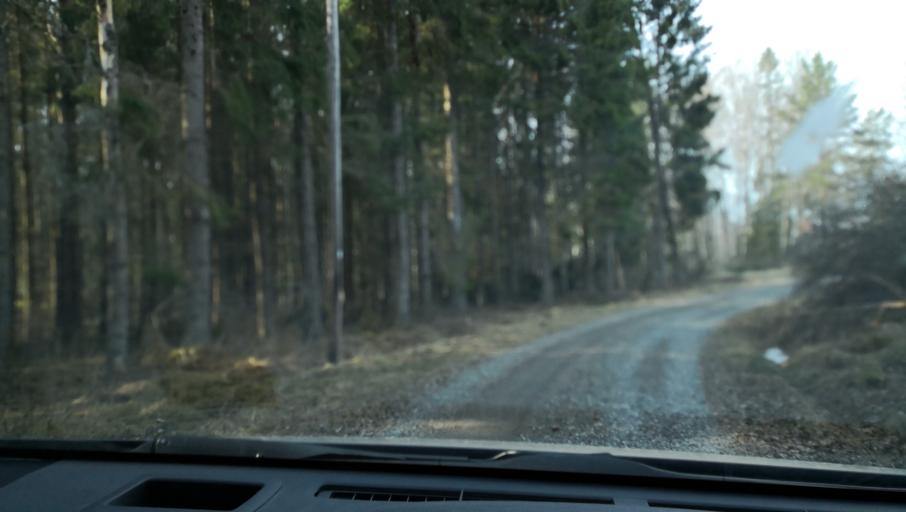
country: SE
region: OErebro
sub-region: Lindesbergs Kommun
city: Frovi
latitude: 59.3859
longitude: 15.4045
